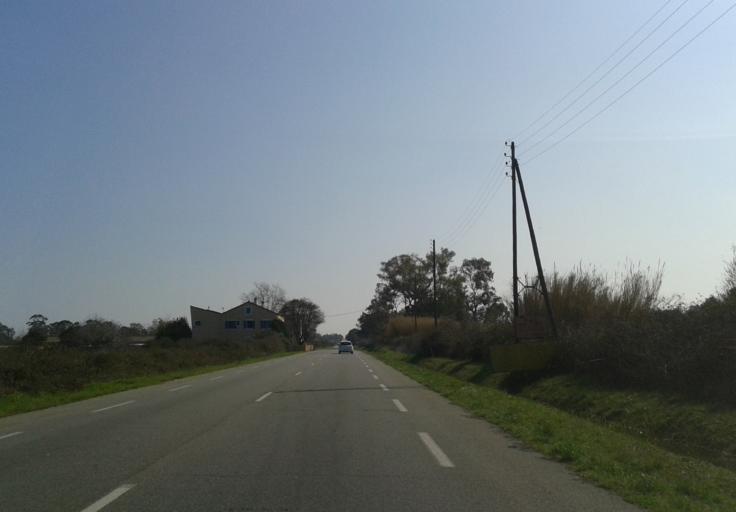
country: FR
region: Corsica
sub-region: Departement de la Haute-Corse
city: San-Nicolao
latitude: 42.3351
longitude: 9.5363
